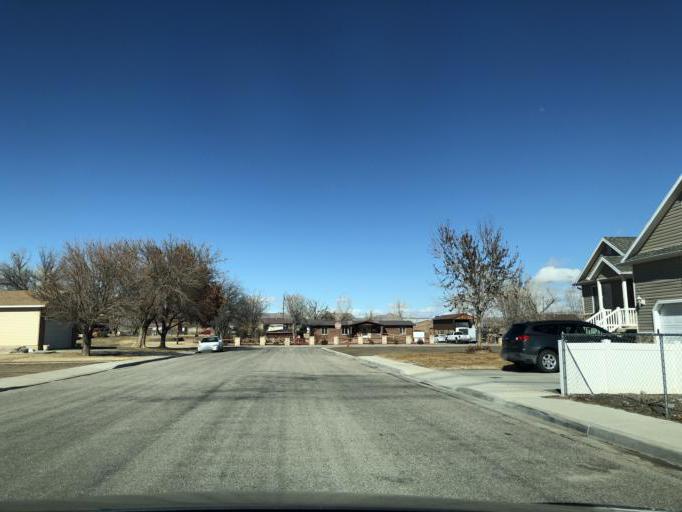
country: US
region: Utah
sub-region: Carbon County
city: East Carbon City
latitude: 38.9985
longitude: -110.1610
